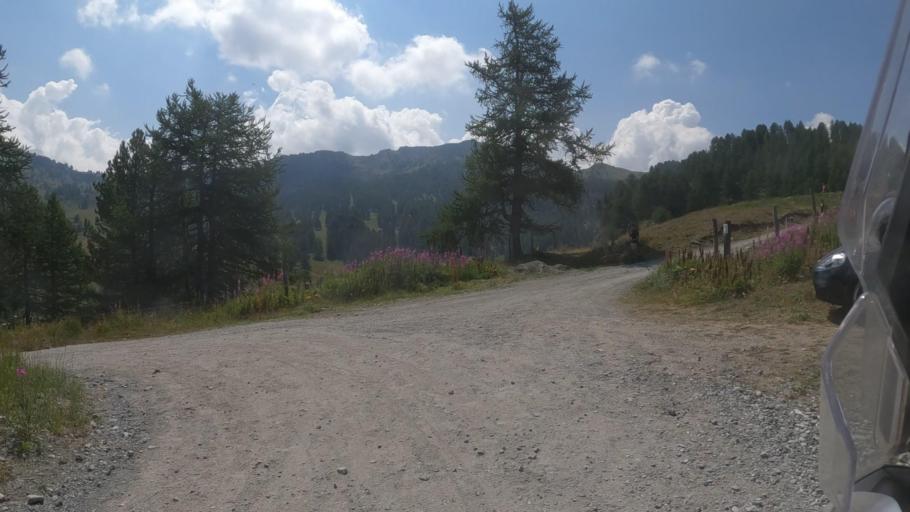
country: IT
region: Piedmont
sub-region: Provincia di Torino
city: Cesana Torinese
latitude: 44.9028
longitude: 6.7925
